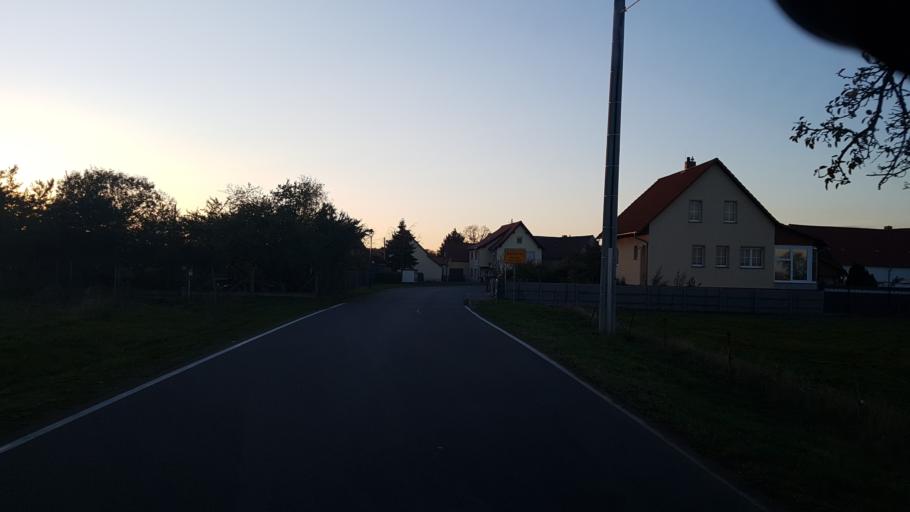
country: DE
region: Saxony
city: Torgau
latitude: 51.4921
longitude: 12.9996
